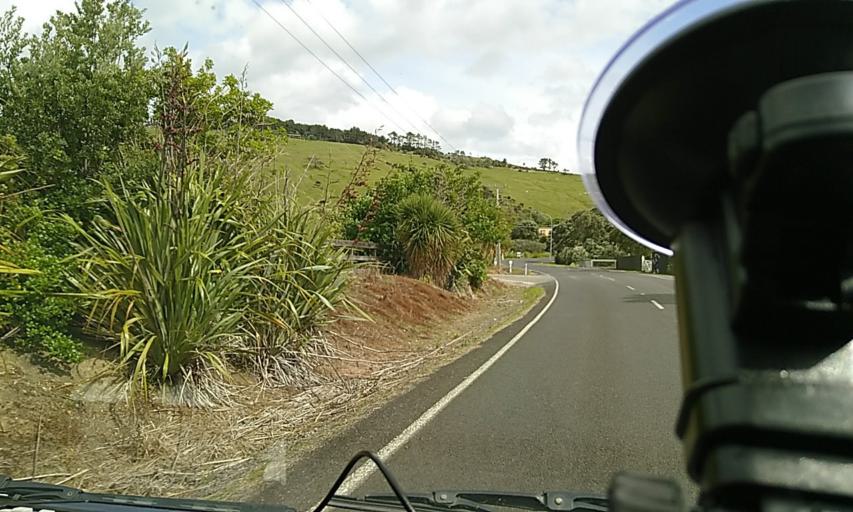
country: NZ
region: Northland
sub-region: Far North District
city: Ahipara
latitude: -35.5300
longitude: 173.3898
